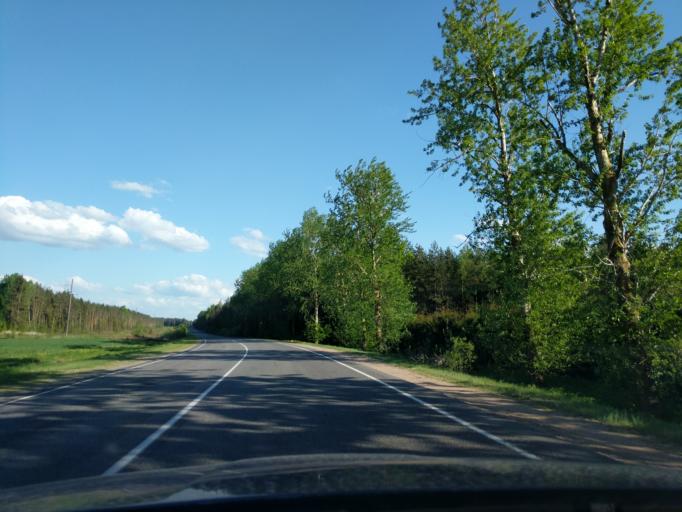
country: BY
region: Minsk
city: Kryvichy
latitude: 54.7528
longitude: 27.1089
